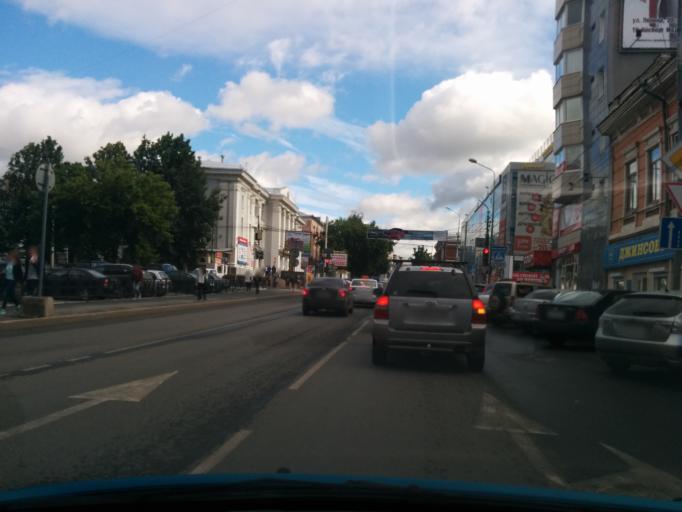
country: RU
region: Perm
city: Perm
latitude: 58.0085
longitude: 56.2352
